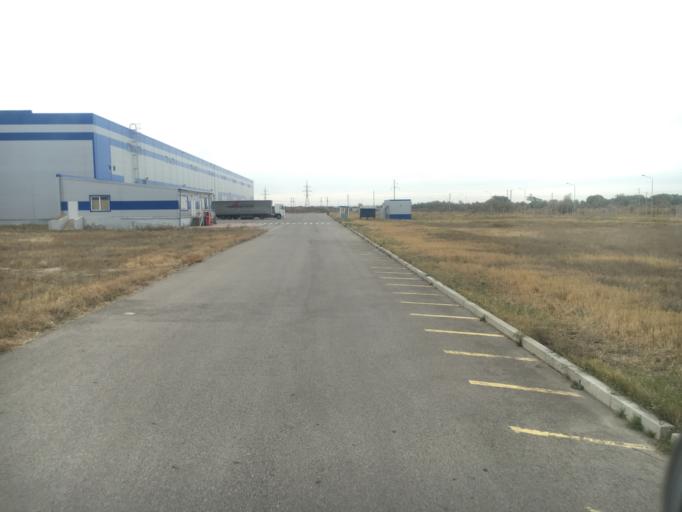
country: KZ
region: Almaty Oblysy
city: Energeticheskiy
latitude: 43.5847
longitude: 77.0966
